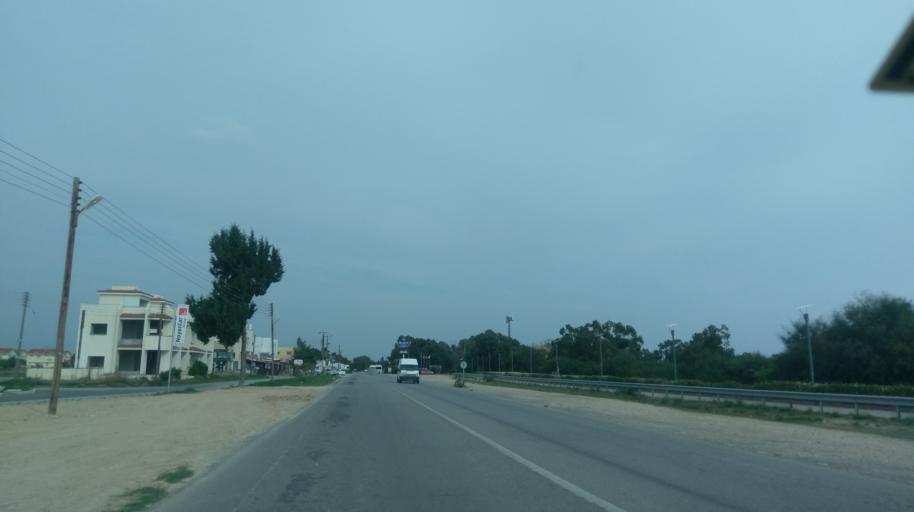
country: CY
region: Ammochostos
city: Trikomo
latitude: 35.2804
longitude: 33.9216
